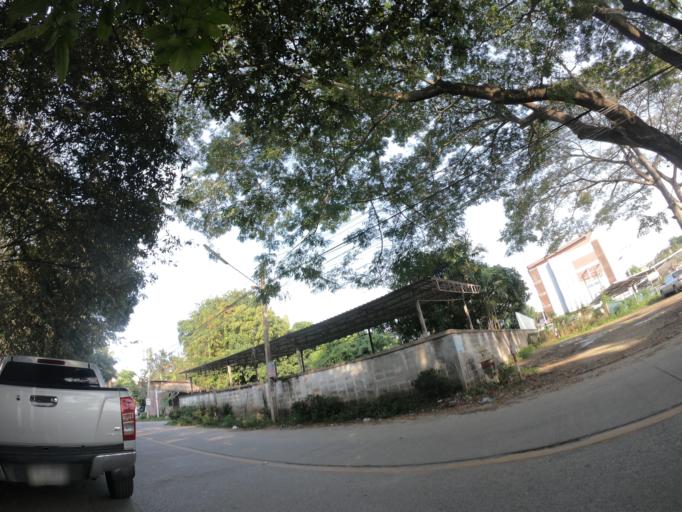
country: TH
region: Chiang Mai
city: Chiang Mai
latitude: 18.8192
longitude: 98.9922
